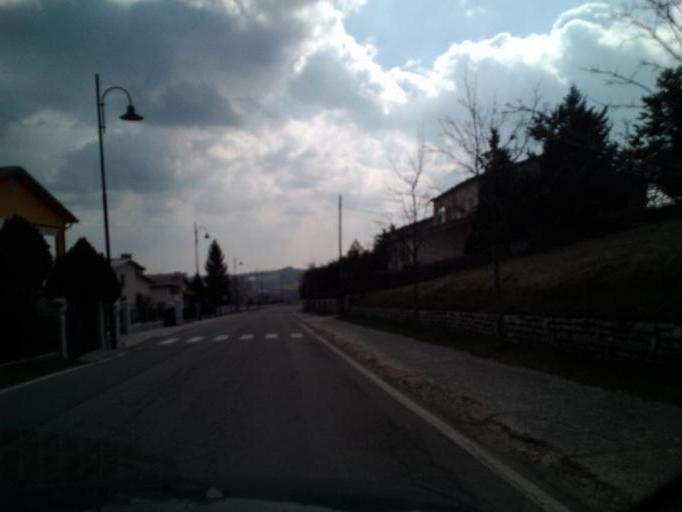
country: IT
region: Veneto
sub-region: Provincia di Verona
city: Sant'Anna d'Alfaedo
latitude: 45.6248
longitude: 10.9510
